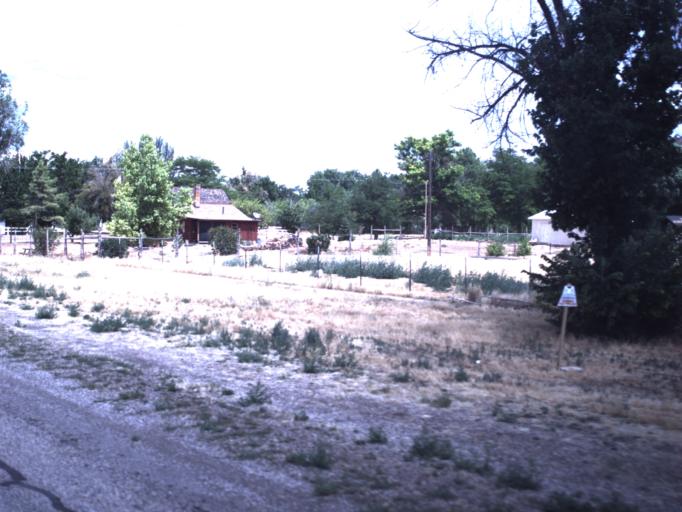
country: US
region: Utah
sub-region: Iron County
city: Parowan
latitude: 37.8837
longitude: -112.7750
